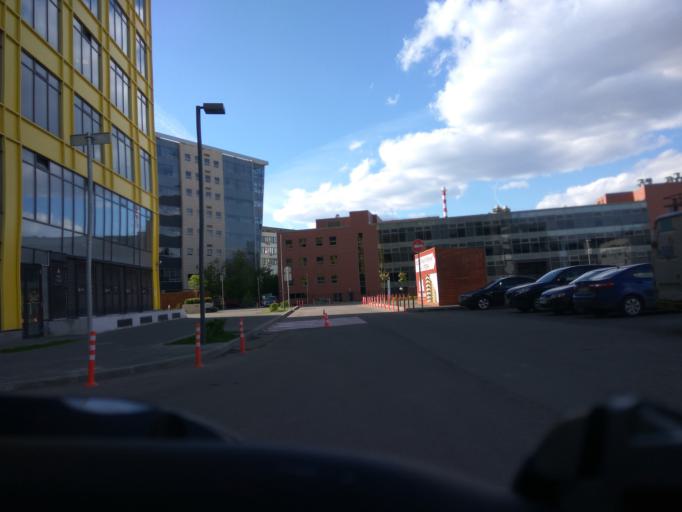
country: RU
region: Moscow
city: Mar'ina Roshcha
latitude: 55.8048
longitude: 37.5906
